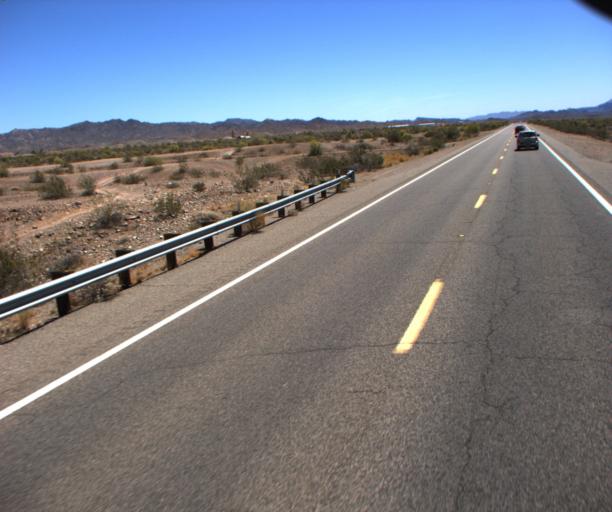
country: US
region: Arizona
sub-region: Mohave County
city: Lake Havasu City
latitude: 34.4205
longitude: -114.2010
